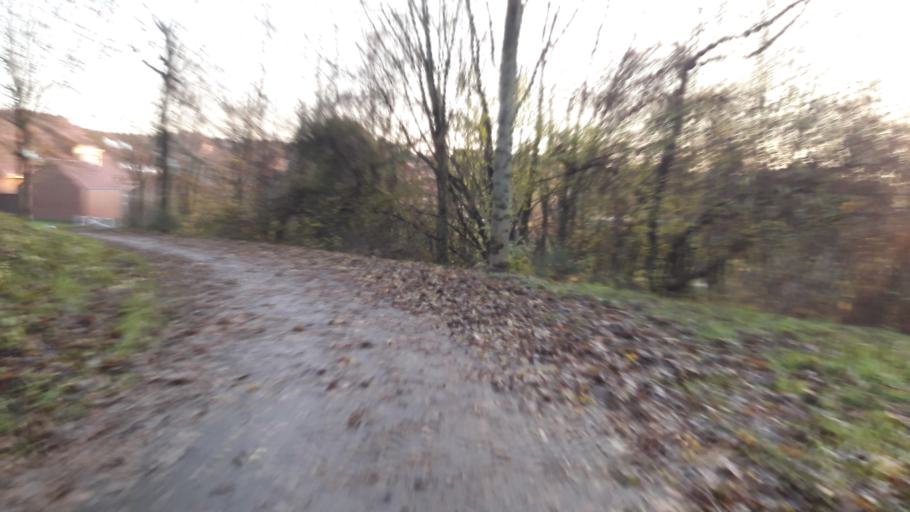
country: DE
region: North Rhine-Westphalia
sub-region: Regierungsbezirk Detmold
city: Paderborn
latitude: 51.7249
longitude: 8.8029
